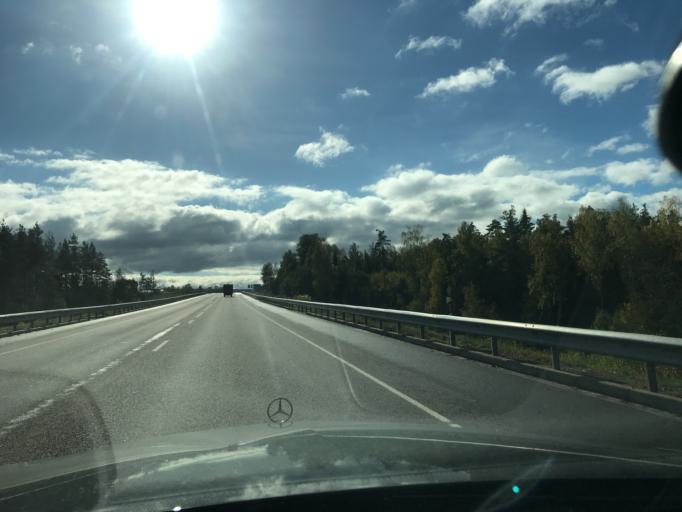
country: EE
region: Vorumaa
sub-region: Voru linn
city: Voru
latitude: 57.8202
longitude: 27.0643
